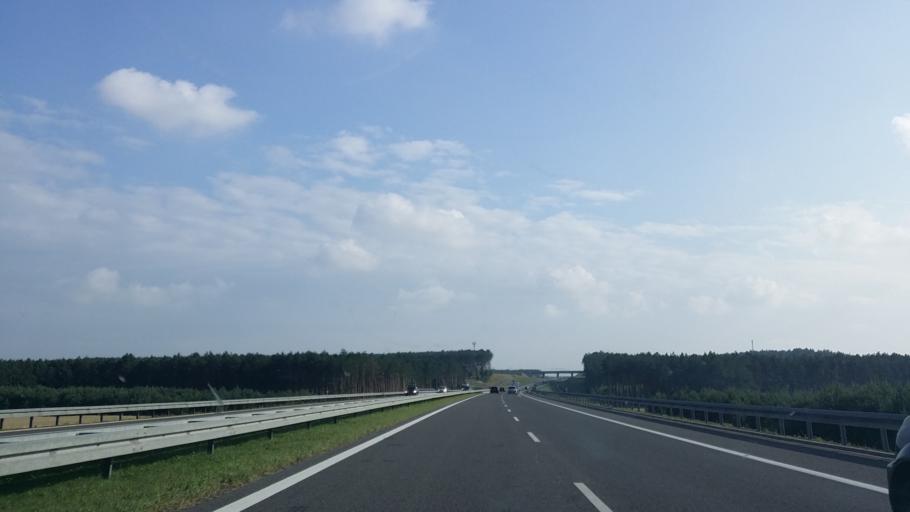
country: PL
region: Lubusz
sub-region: Powiat swiebodzinski
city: Swiebodzin
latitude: 52.3327
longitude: 15.5563
